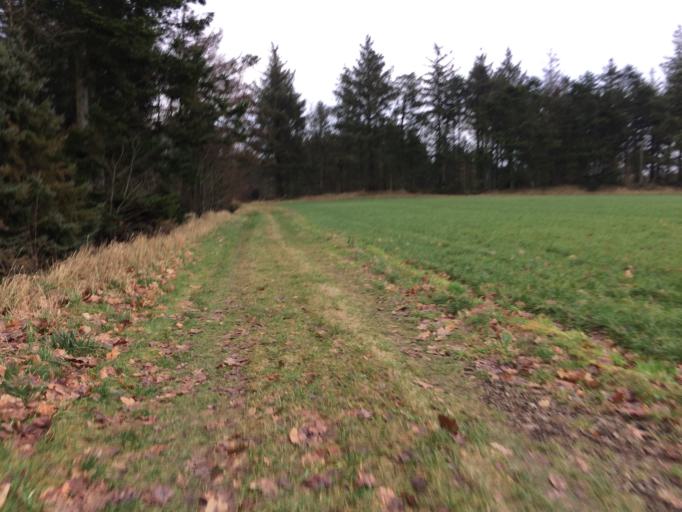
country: DK
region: Central Jutland
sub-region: Holstebro Kommune
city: Ulfborg
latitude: 56.2637
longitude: 8.2568
